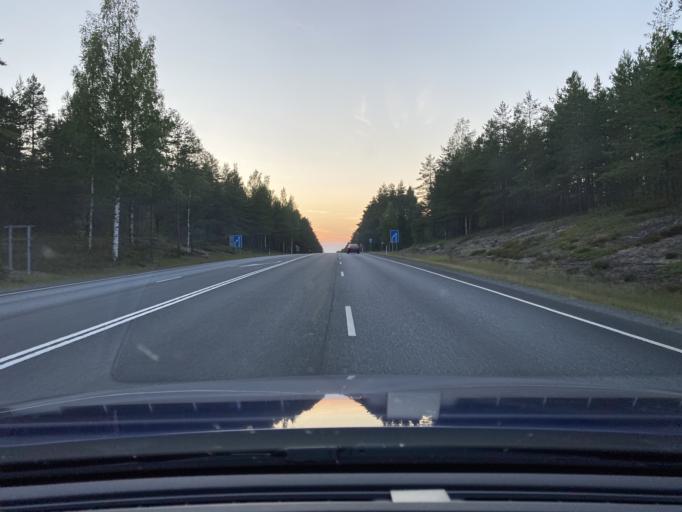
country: FI
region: Pirkanmaa
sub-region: Luoteis-Pirkanmaa
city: Ikaalinen
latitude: 61.7825
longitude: 22.9992
